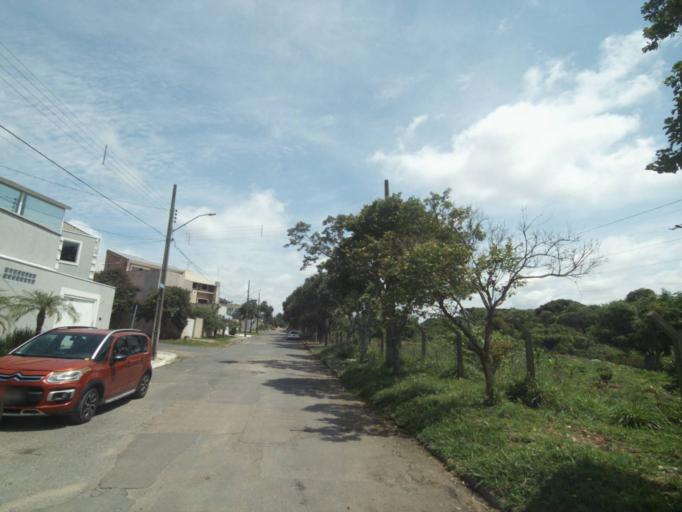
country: BR
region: Parana
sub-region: Curitiba
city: Curitiba
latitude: -25.4572
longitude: -49.3563
